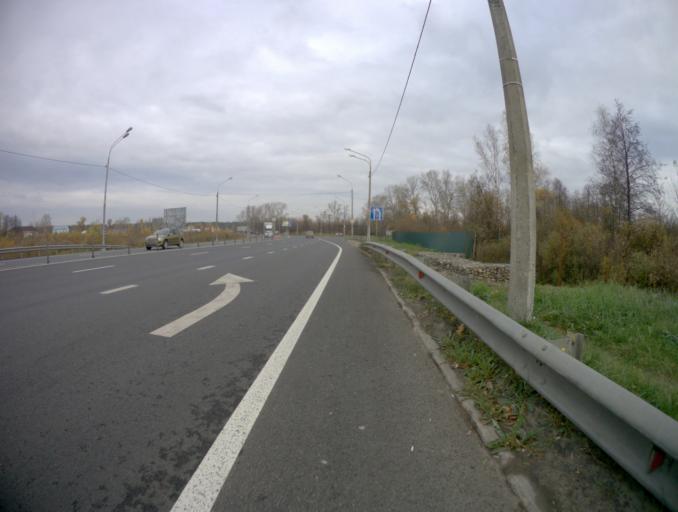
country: RU
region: Moskovskaya
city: Orekhovo-Zuyevo
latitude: 55.8393
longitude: 38.9706
